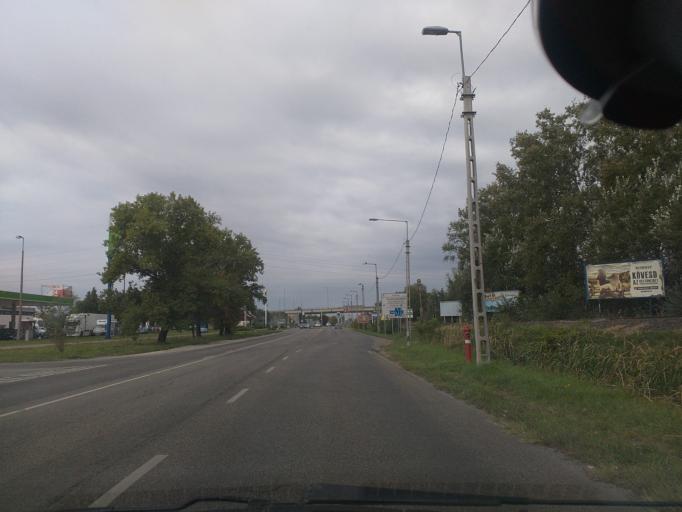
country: HU
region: Budapest
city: Budapest XVIII. keruelet
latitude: 47.4234
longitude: 19.1606
